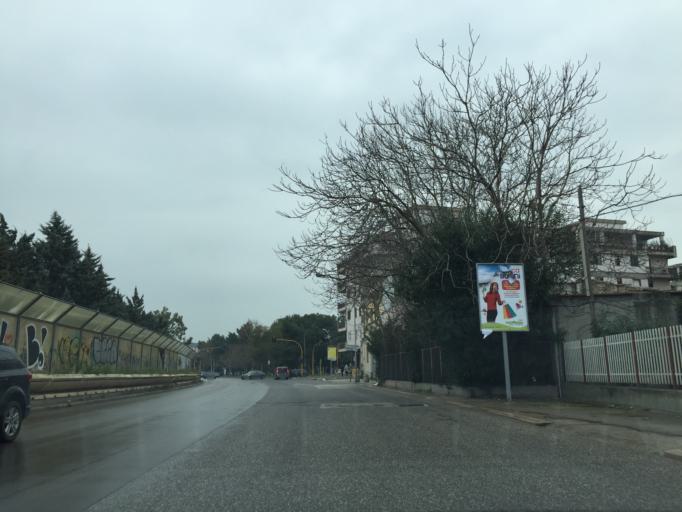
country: IT
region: Apulia
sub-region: Provincia di Foggia
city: Foggia
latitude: 41.4650
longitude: 15.5333
